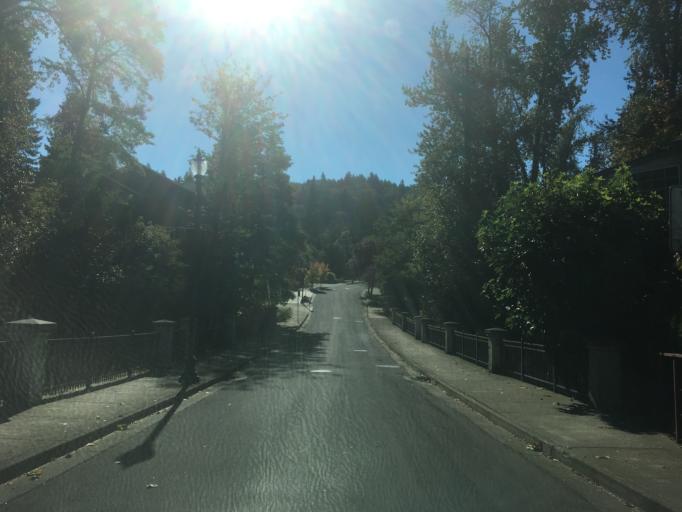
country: US
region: Oregon
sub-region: Multnomah County
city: Gresham
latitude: 45.4806
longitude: -122.4248
